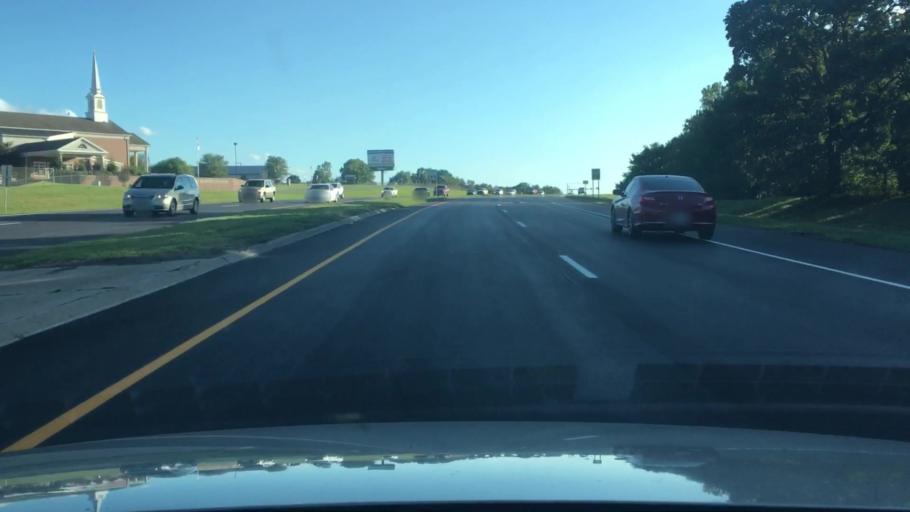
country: US
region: Oklahoma
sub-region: Cherokee County
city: Tahlequah
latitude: 35.9121
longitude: -94.9556
